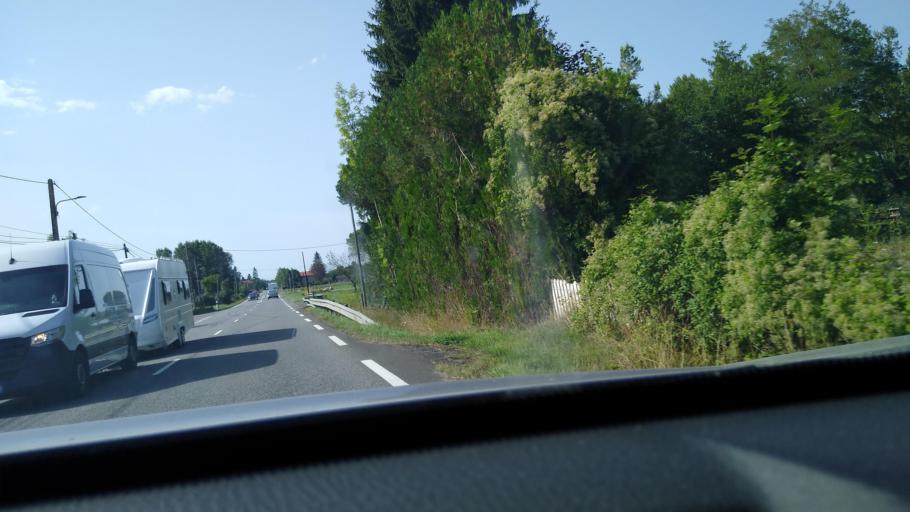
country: FR
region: Midi-Pyrenees
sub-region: Departement de la Haute-Garonne
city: Salies-du-Salat
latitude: 43.0505
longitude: 0.9837
